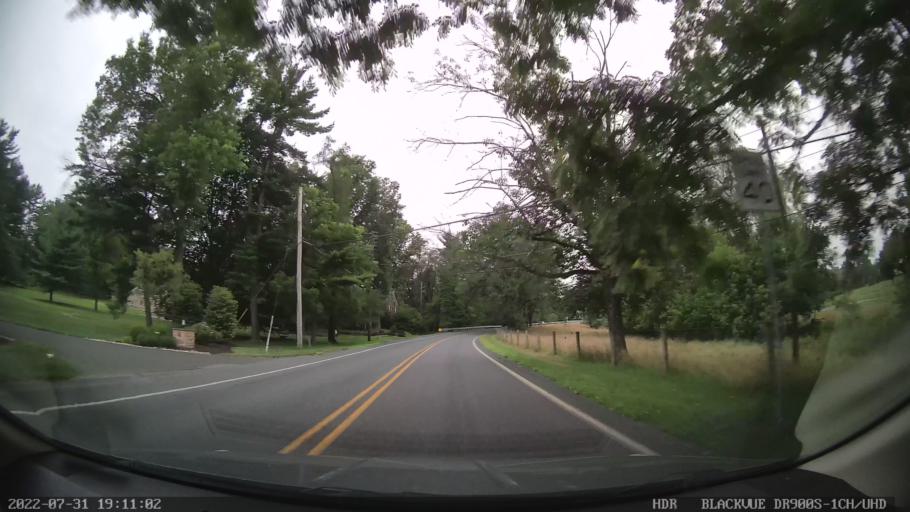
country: US
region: Pennsylvania
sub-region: Northampton County
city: Hellertown
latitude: 40.5722
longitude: -75.3729
